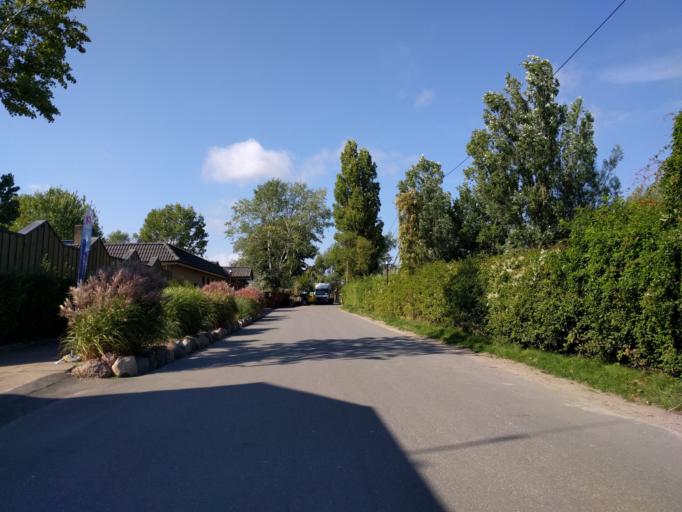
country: DE
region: Schleswig-Holstein
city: Burg auf Fehmarn
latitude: 54.4044
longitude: 11.1791
